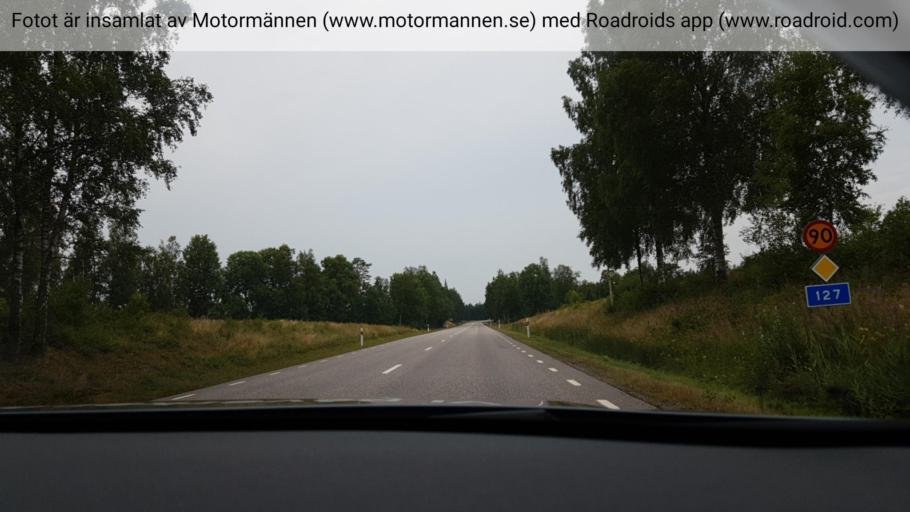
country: SE
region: Joenkoeping
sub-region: Varnamo Kommun
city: Bor
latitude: 57.2731
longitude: 14.2371
